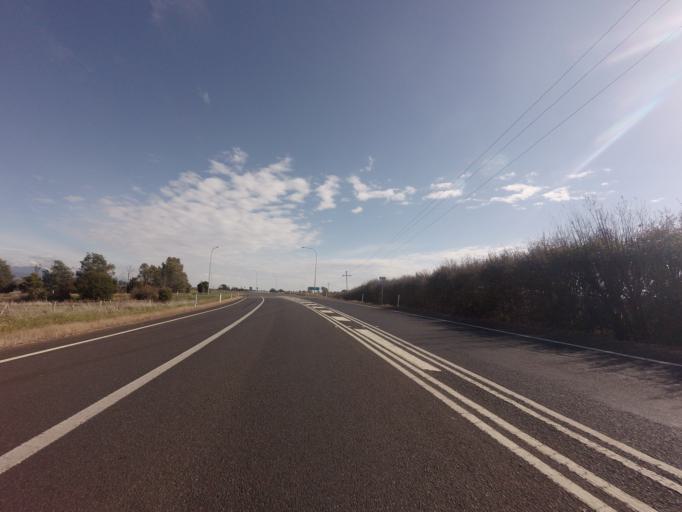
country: AU
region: Tasmania
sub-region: Meander Valley
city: Westbury
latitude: -41.5261
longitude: 146.8769
